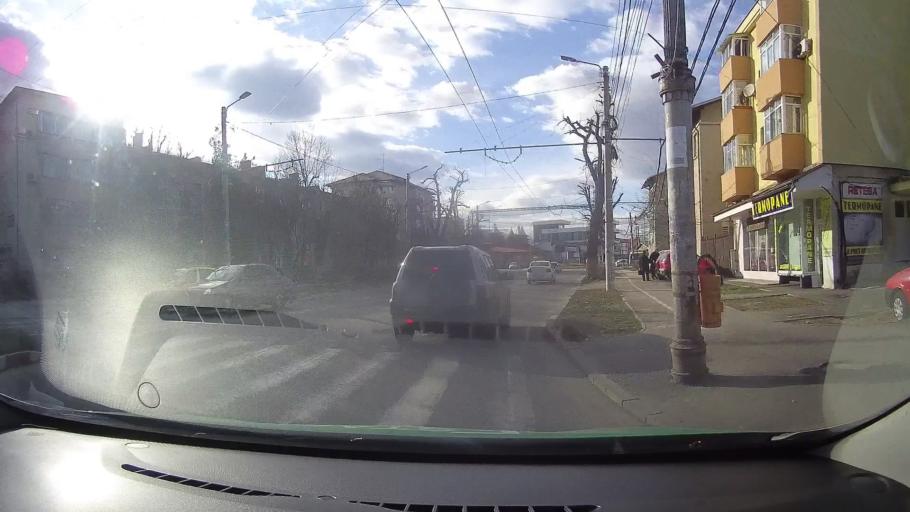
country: RO
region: Dambovita
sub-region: Comuna Lucieni
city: Lucieni
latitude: 44.8603
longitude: 25.4160
